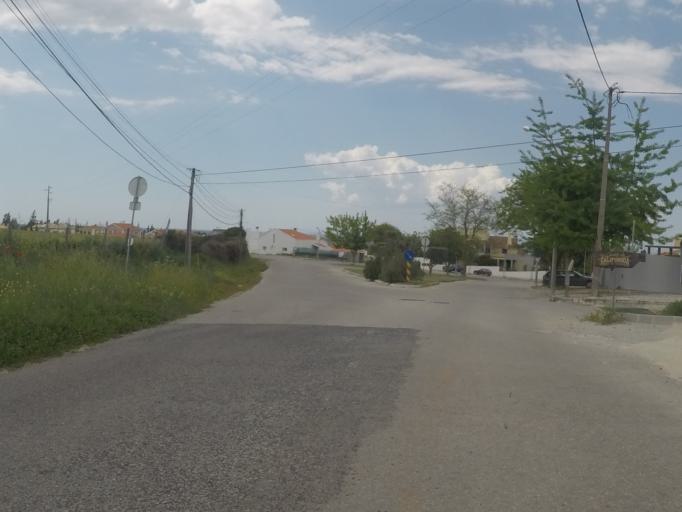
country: PT
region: Setubal
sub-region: Palmela
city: Quinta do Anjo
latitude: 38.5151
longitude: -9.0079
